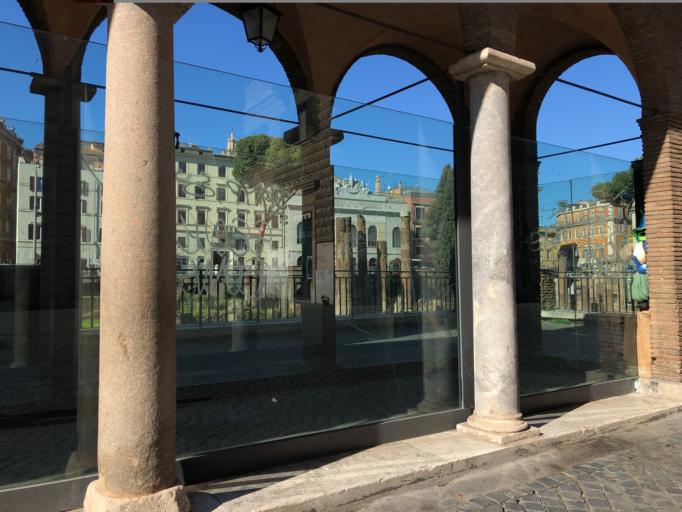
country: VA
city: Vatican City
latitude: 41.8950
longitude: 12.4773
